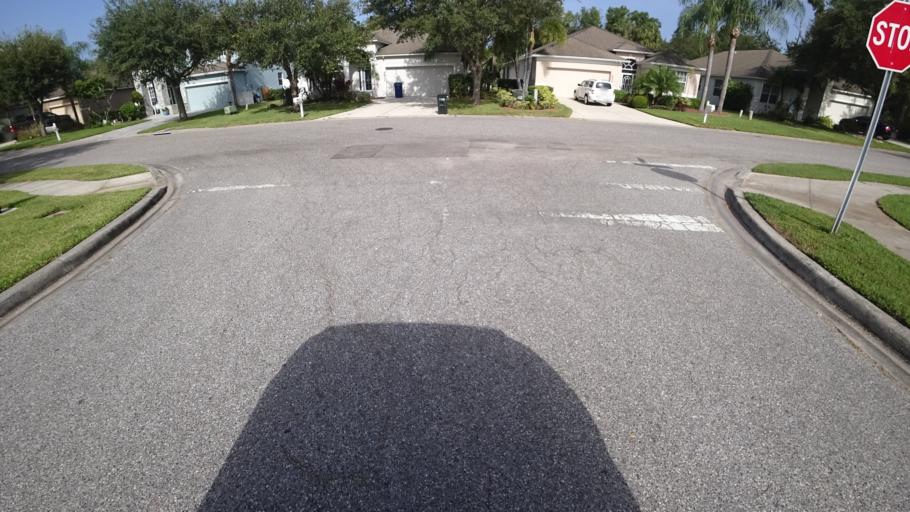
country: US
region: Florida
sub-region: Manatee County
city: Ellenton
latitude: 27.5574
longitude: -82.4968
